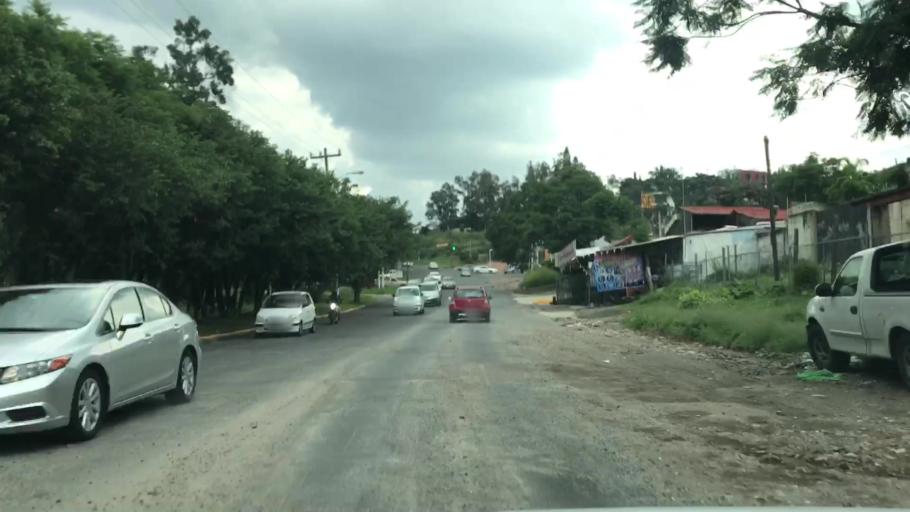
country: MX
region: Jalisco
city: Guadalajara
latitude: 20.6208
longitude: -103.4084
